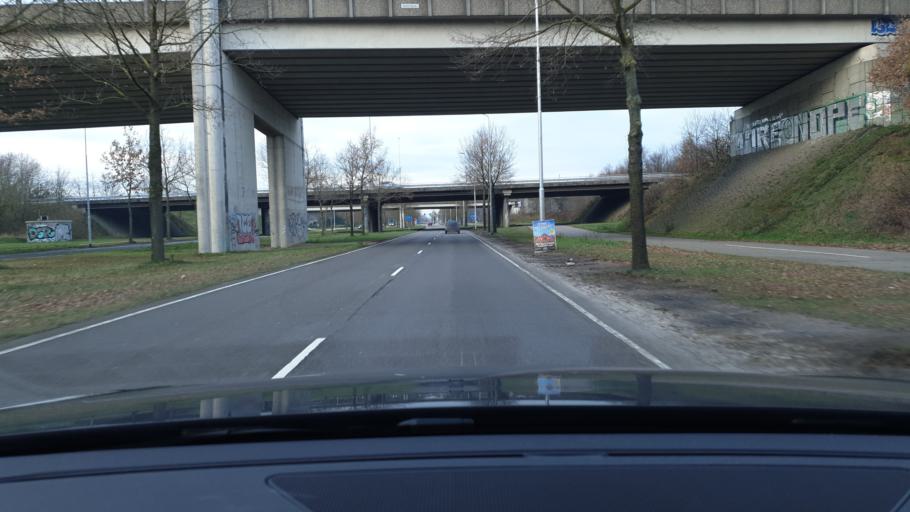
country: NL
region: North Brabant
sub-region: Gemeente Best
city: Best
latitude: 51.4881
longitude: 5.4287
